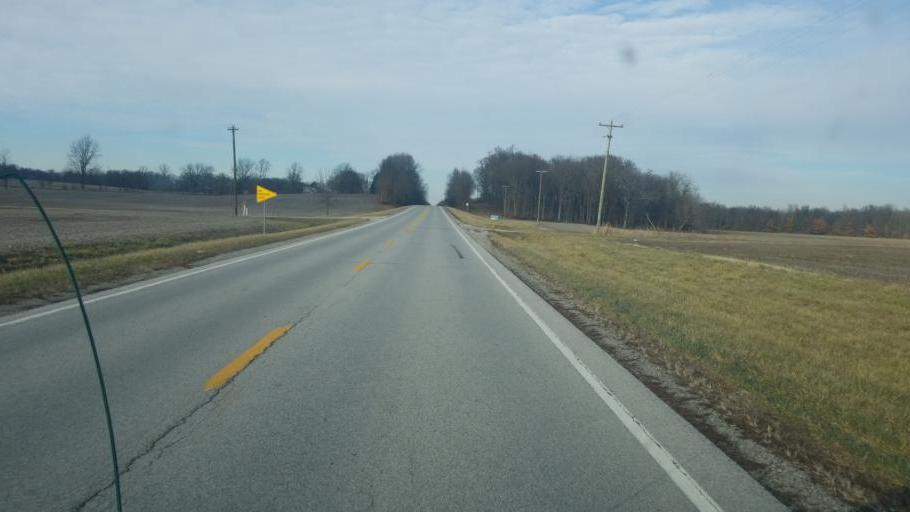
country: US
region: Illinois
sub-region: Wabash County
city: Mount Carmel
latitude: 38.5567
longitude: -87.6948
